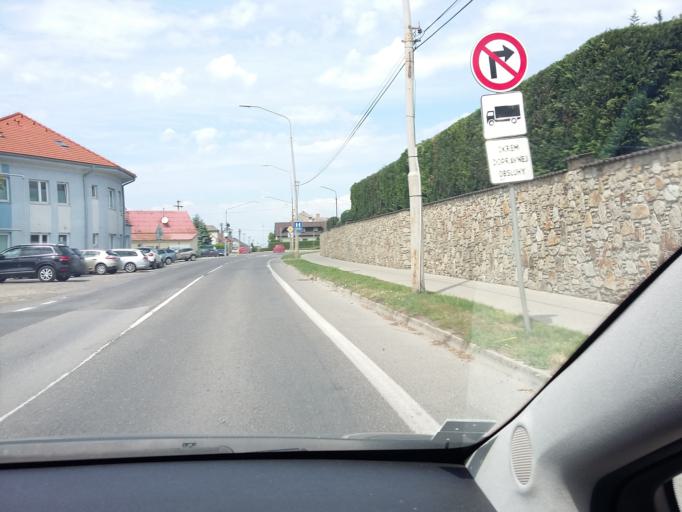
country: SK
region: Bratislavsky
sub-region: Okres Malacky
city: Malacky
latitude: 48.4397
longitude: 17.0251
